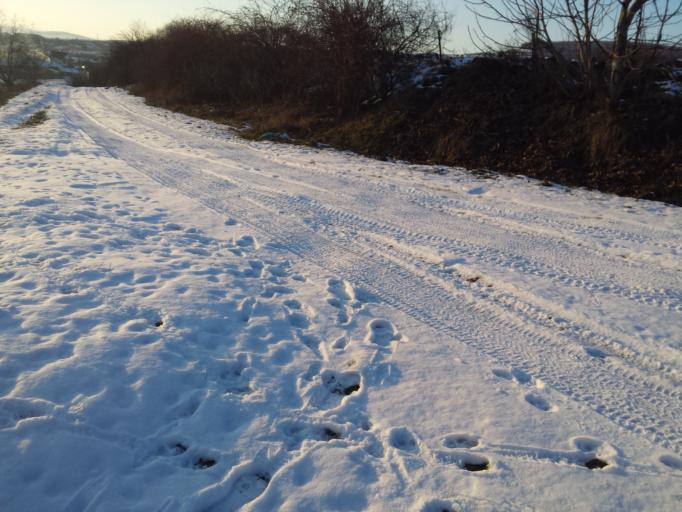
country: RO
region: Cluj
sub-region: Municipiul Cluj-Napoca
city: Cluj-Napoca
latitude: 46.7964
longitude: 23.5842
